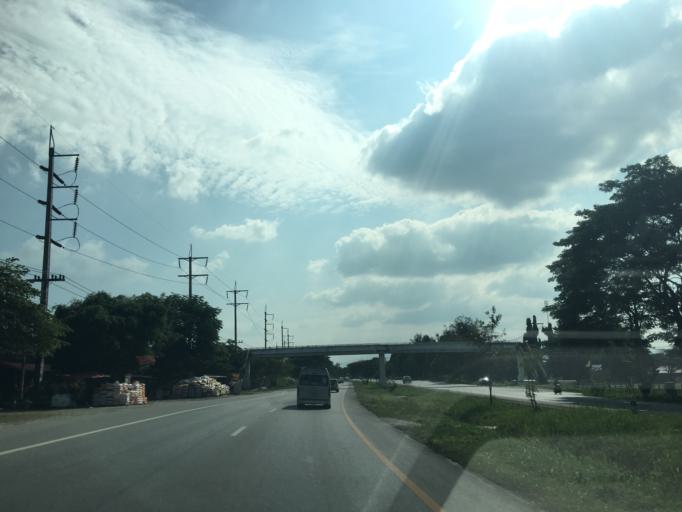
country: TH
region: Chiang Rai
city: Mae Lao
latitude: 19.7083
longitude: 99.7201
